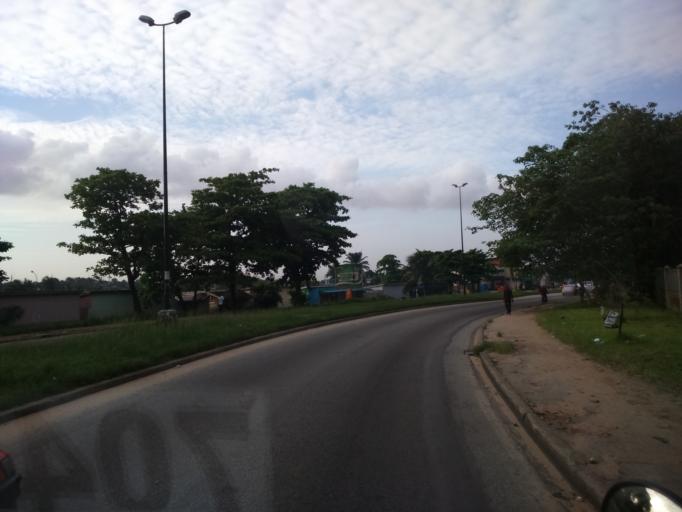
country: CI
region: Lagunes
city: Abobo
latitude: 5.3664
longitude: -3.9977
